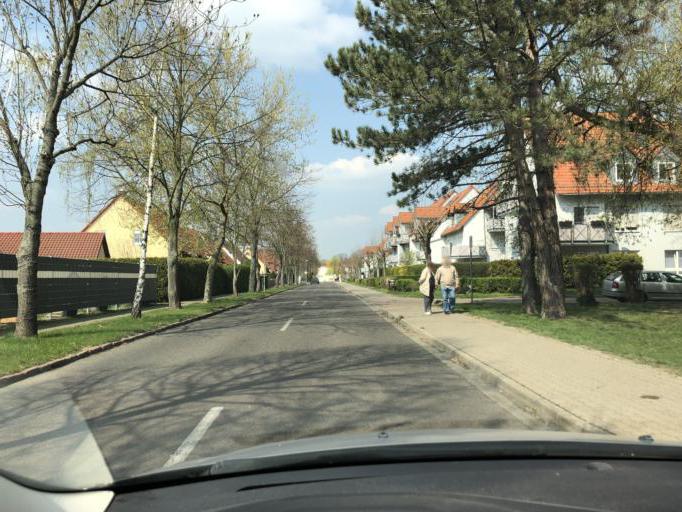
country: DE
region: Saxony-Anhalt
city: Landsberg
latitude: 51.5298
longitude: 12.1508
